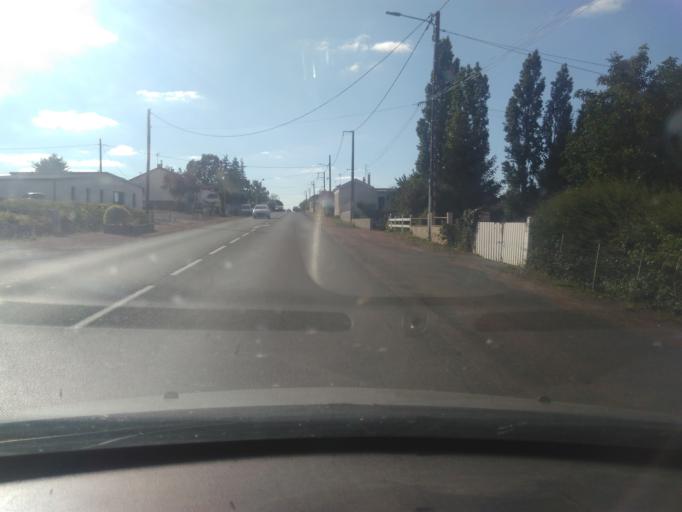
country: FR
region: Pays de la Loire
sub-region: Departement de la Vendee
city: Saint-Florent-des-Bois
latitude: 46.5987
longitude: -1.3246
